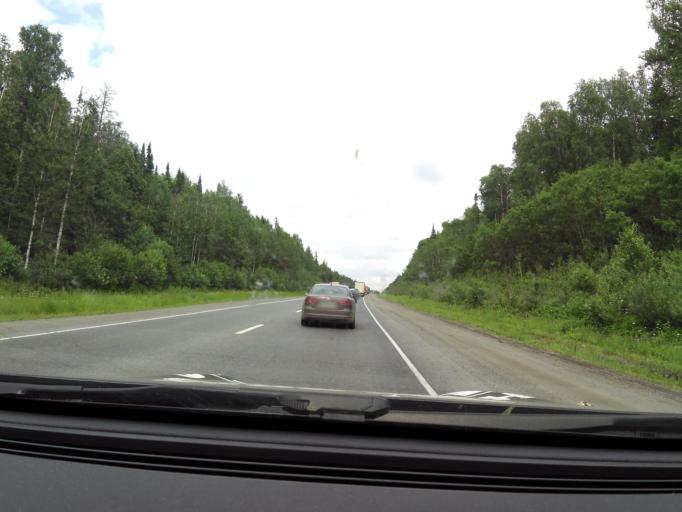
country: RU
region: Sverdlovsk
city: Bilimbay
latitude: 56.8530
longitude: 59.6990
